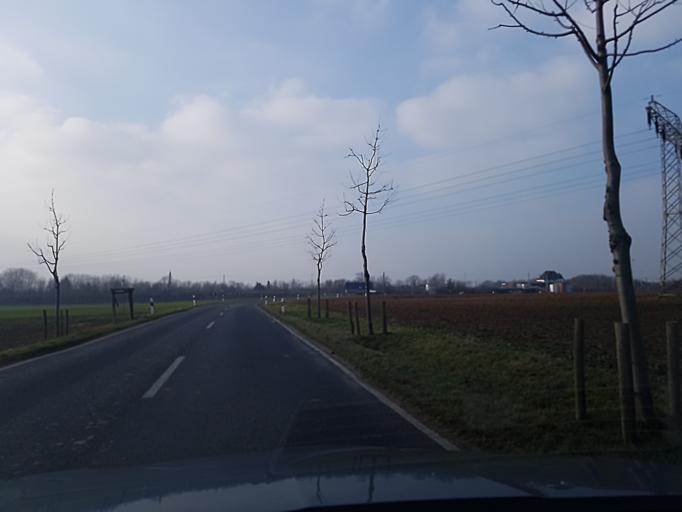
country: DE
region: Brandenburg
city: Doberlug-Kirchhain
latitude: 51.6179
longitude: 13.5690
